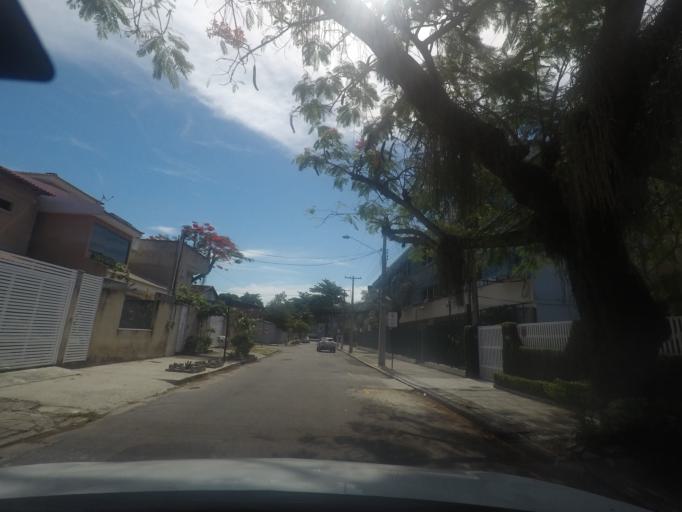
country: BR
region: Rio de Janeiro
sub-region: Niteroi
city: Niteroi
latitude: -22.9169
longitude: -43.0888
